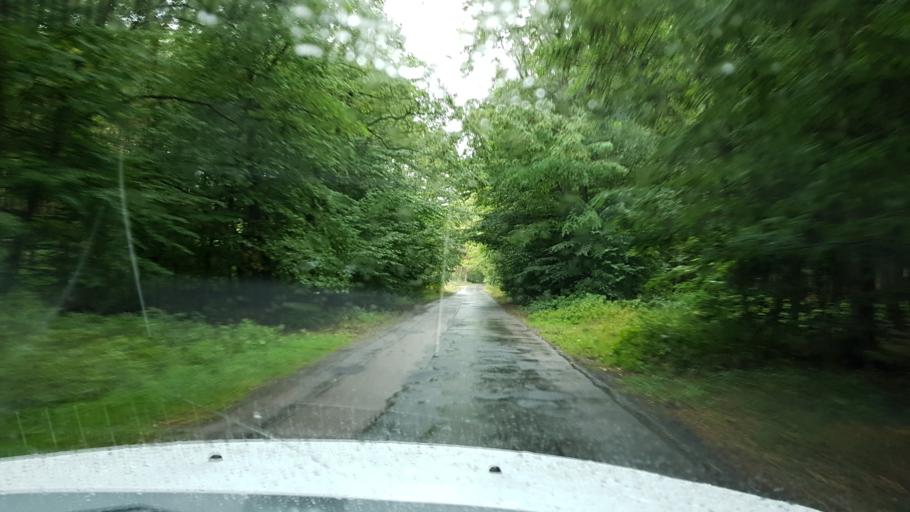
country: DE
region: Brandenburg
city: Meyenburg
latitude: 52.9843
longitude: 14.2623
